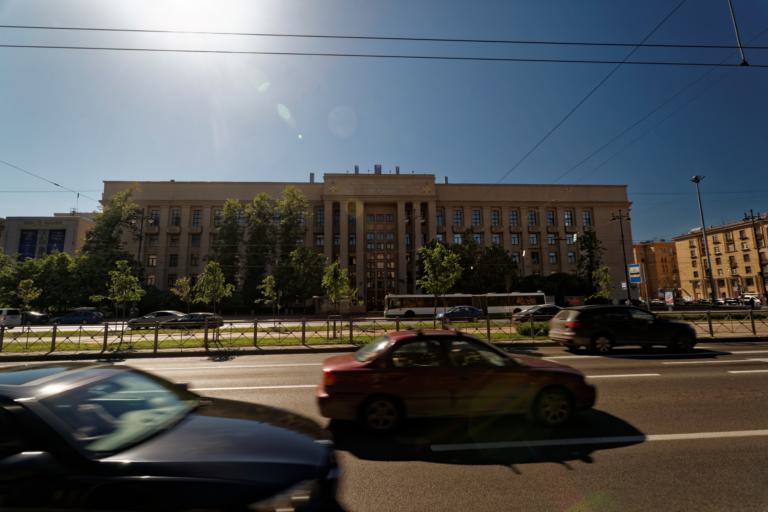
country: RU
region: St.-Petersburg
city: Kupchino
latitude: 59.8751
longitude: 30.3206
